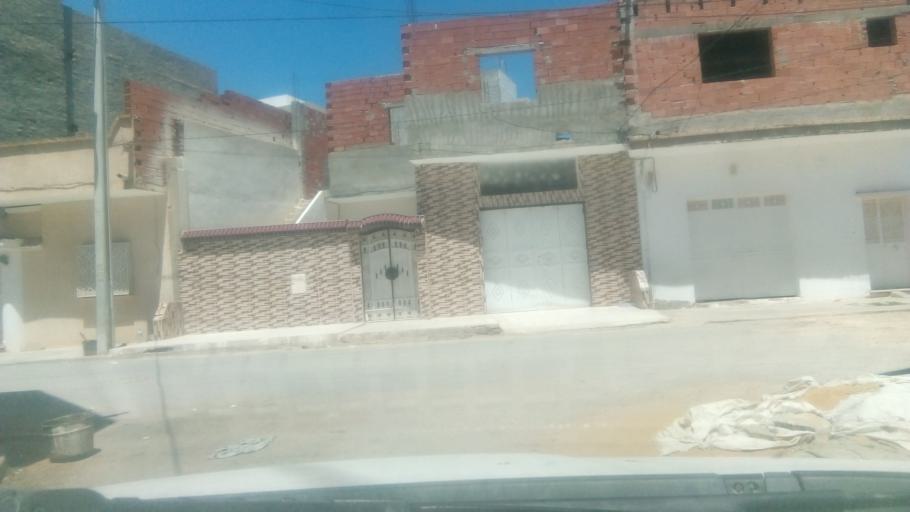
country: TN
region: Al Qayrawan
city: Kairouan
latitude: 35.6661
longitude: 10.0846
